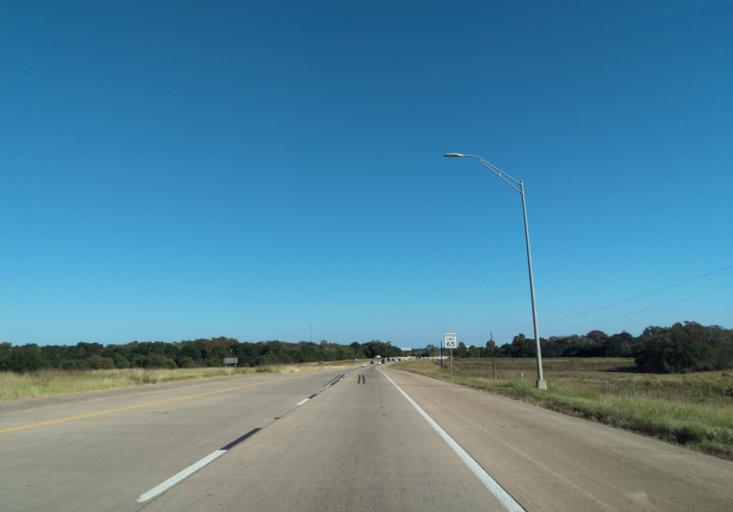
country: US
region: Texas
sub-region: Waller County
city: Hempstead
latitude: 30.1126
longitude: -96.0611
